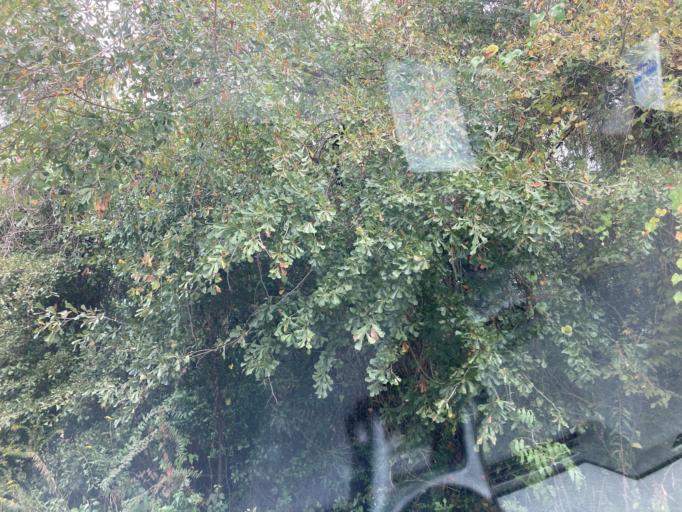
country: US
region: Mississippi
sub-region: Lamar County
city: West Hattiesburg
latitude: 31.2827
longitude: -89.3497
